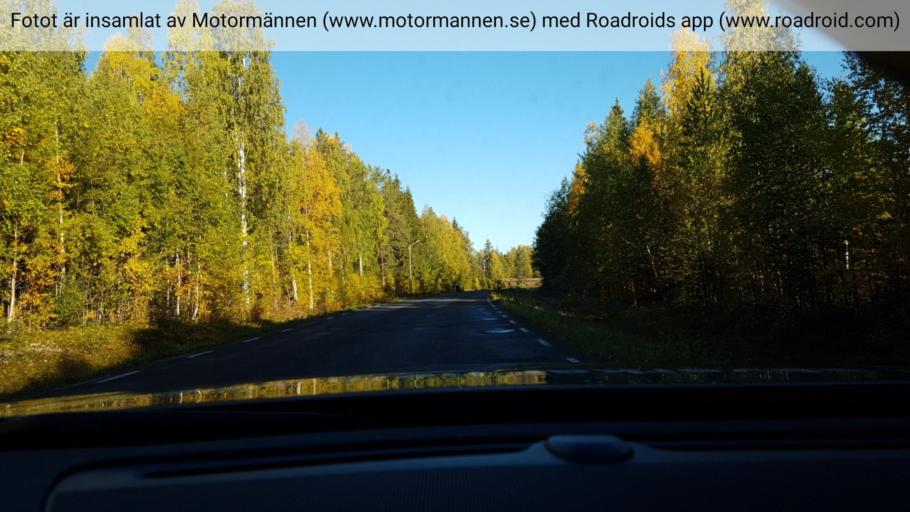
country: SE
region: Norrbotten
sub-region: Bodens Kommun
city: Boden
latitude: 65.9554
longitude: 21.6006
